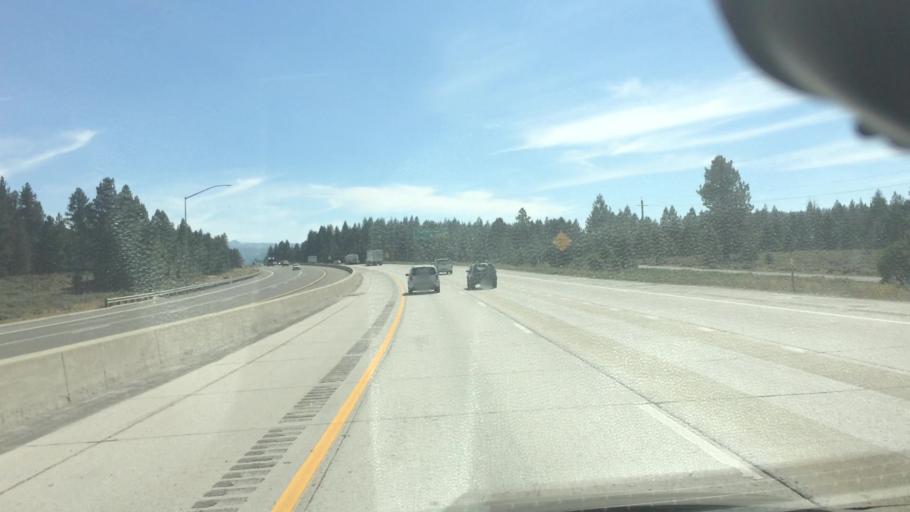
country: US
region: California
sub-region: Nevada County
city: Truckee
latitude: 39.3583
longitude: -120.1421
